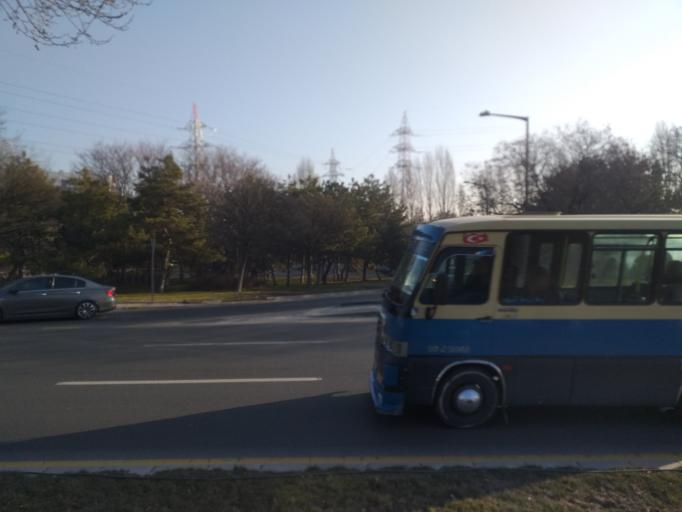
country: TR
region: Ankara
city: Ankara
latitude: 39.9537
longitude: 32.8210
